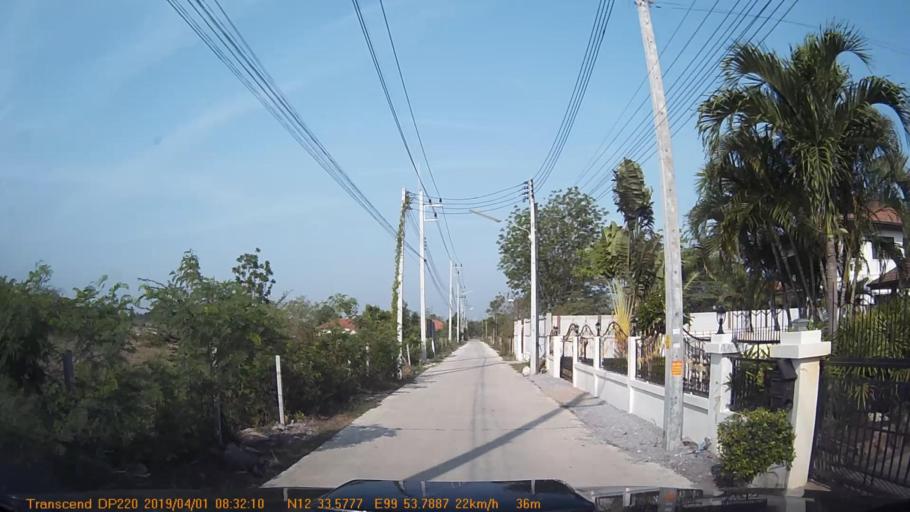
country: TH
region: Prachuap Khiri Khan
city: Hua Hin
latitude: 12.5596
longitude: 99.8964
